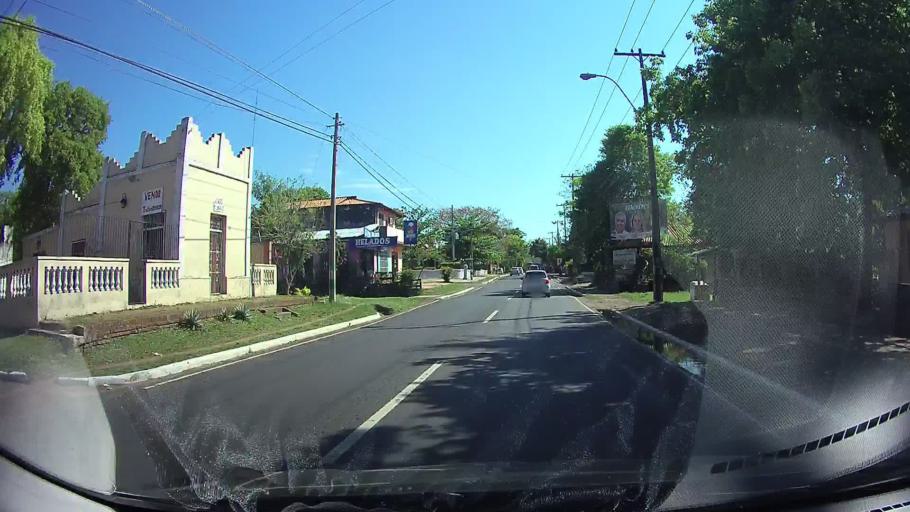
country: PY
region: Central
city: Ypacarai
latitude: -25.4007
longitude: -57.2885
